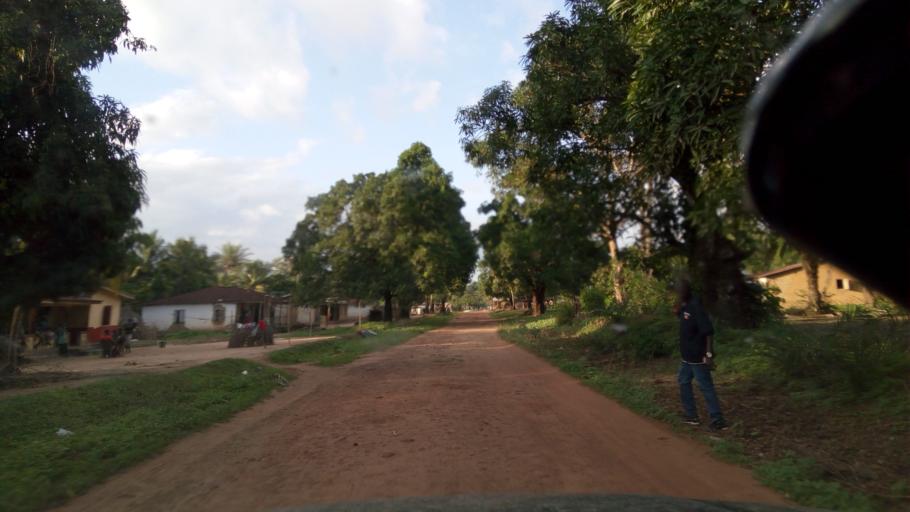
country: SL
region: Northern Province
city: Konakridee
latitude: 8.7750
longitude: -13.1369
